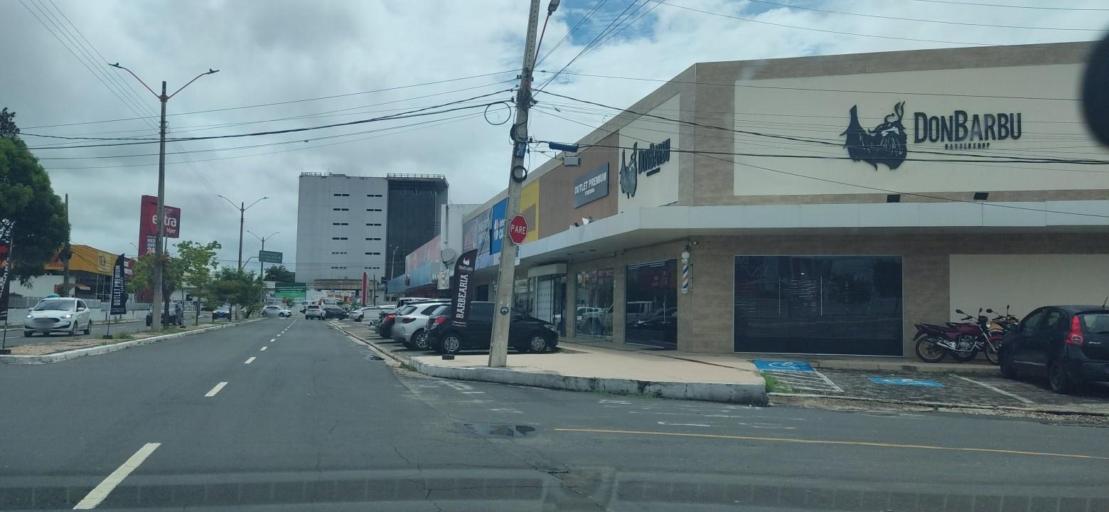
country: BR
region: Piaui
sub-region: Teresina
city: Teresina
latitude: -5.0720
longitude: -42.7733
